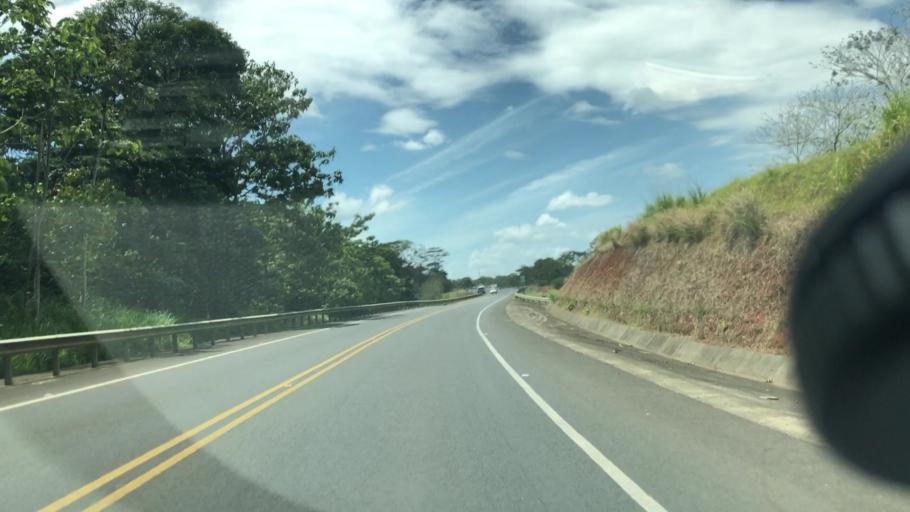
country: CR
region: Heredia
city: La Virgen
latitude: 10.4409
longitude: -84.1535
